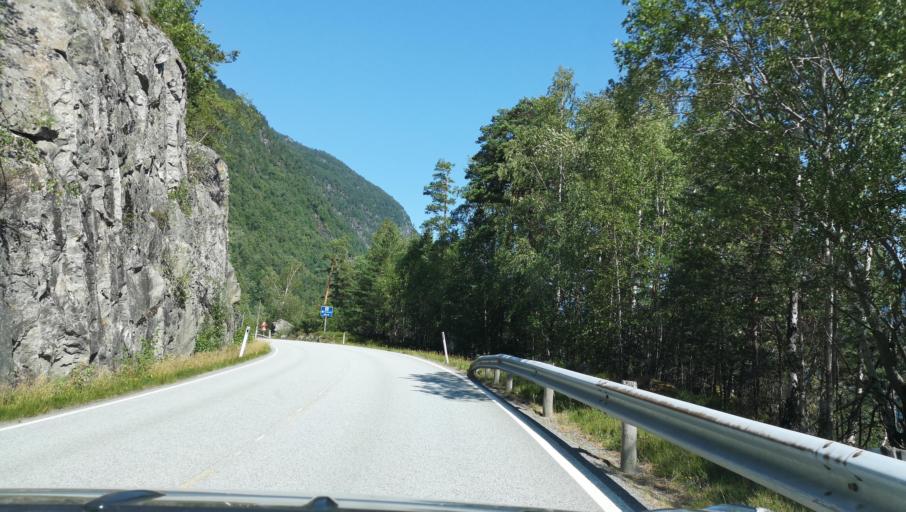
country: NO
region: Hordaland
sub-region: Ulvik
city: Ulvik
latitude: 60.4910
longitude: 6.8927
